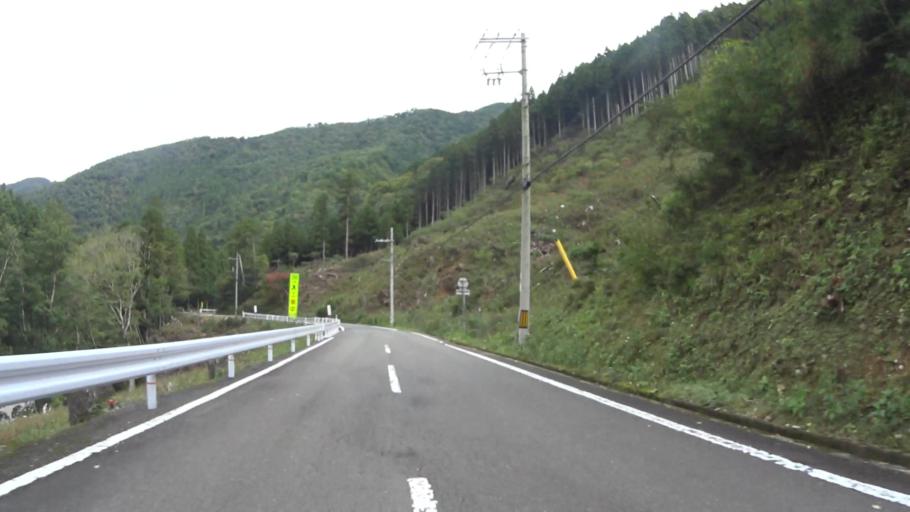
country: JP
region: Fukui
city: Obama
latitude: 35.3161
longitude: 135.6880
